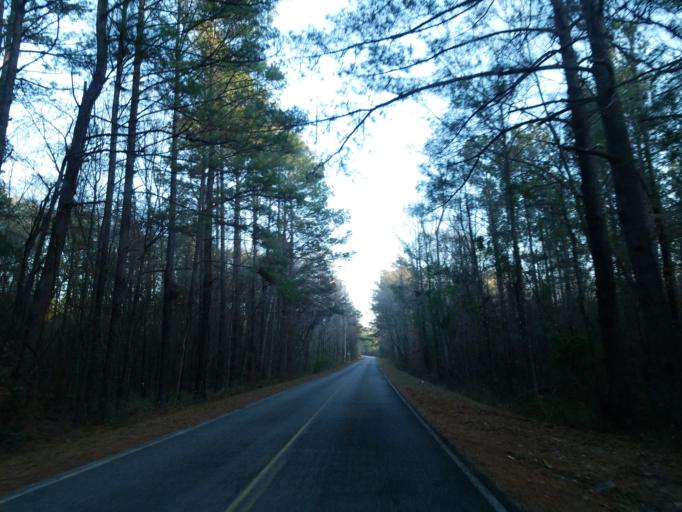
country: US
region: Mississippi
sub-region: Lauderdale County
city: Meridian
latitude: 32.2673
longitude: -88.7870
